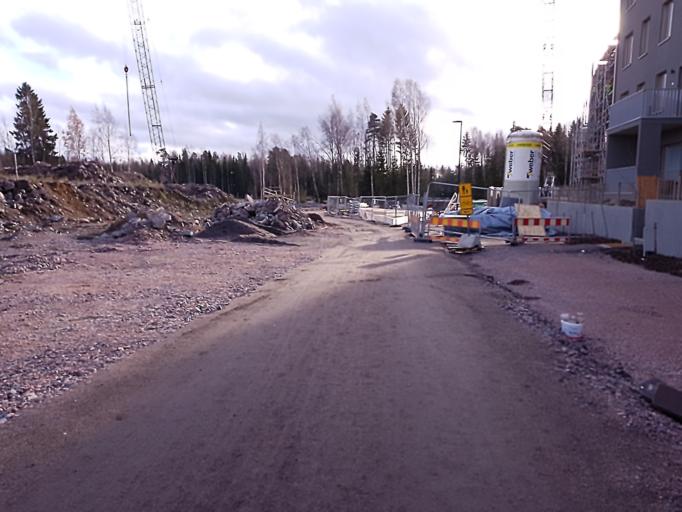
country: FI
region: Uusimaa
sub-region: Helsinki
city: Teekkarikylae
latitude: 60.2613
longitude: 24.8938
